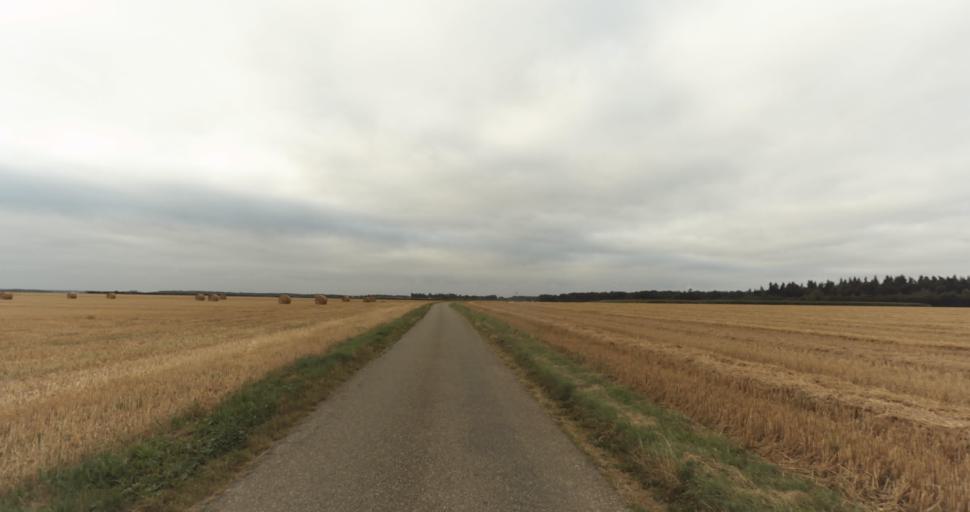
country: FR
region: Haute-Normandie
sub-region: Departement de l'Eure
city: Saint-Germain-sur-Avre
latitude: 48.7898
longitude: 1.2606
